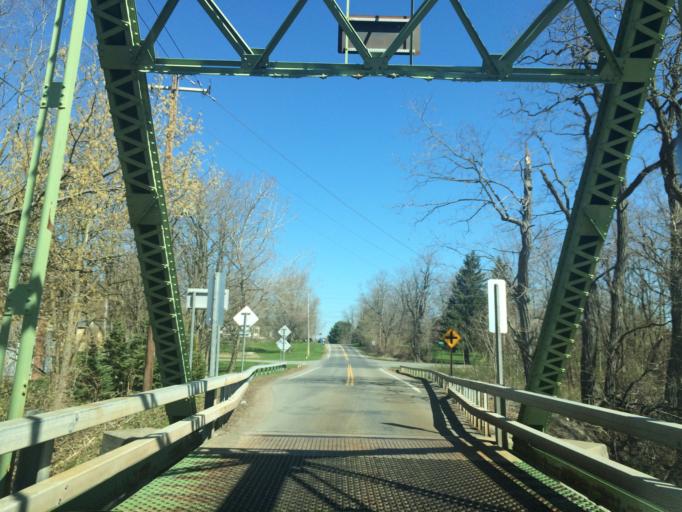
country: US
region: New York
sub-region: Wayne County
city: Palmyra
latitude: 43.0637
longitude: -77.2582
